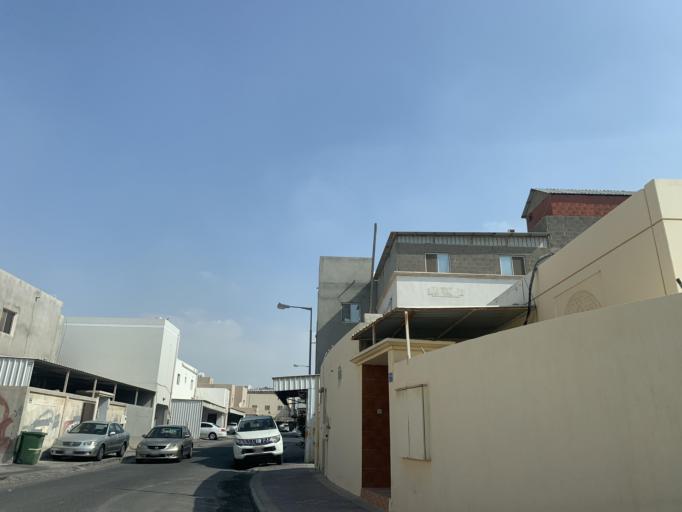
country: BH
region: Central Governorate
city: Madinat Hamad
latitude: 26.1291
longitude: 50.4946
